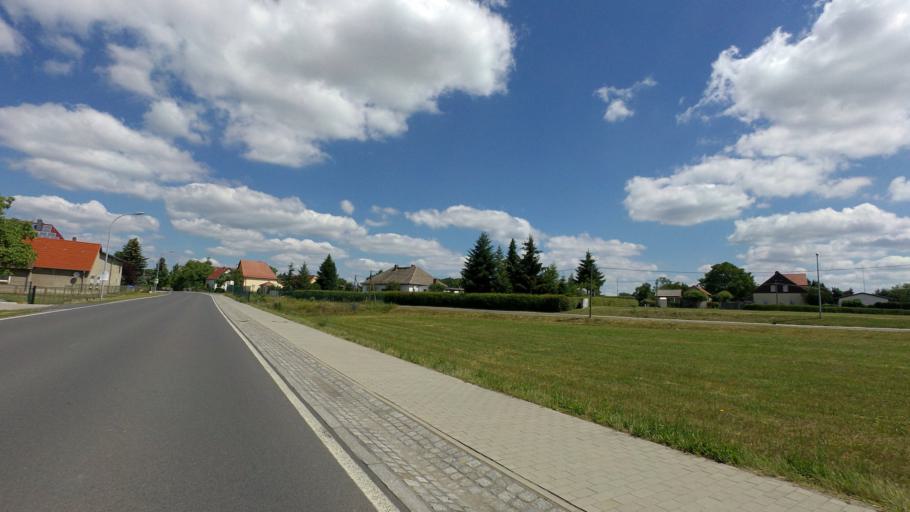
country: DE
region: Brandenburg
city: Sonnewalde
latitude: 51.6857
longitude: 13.6476
